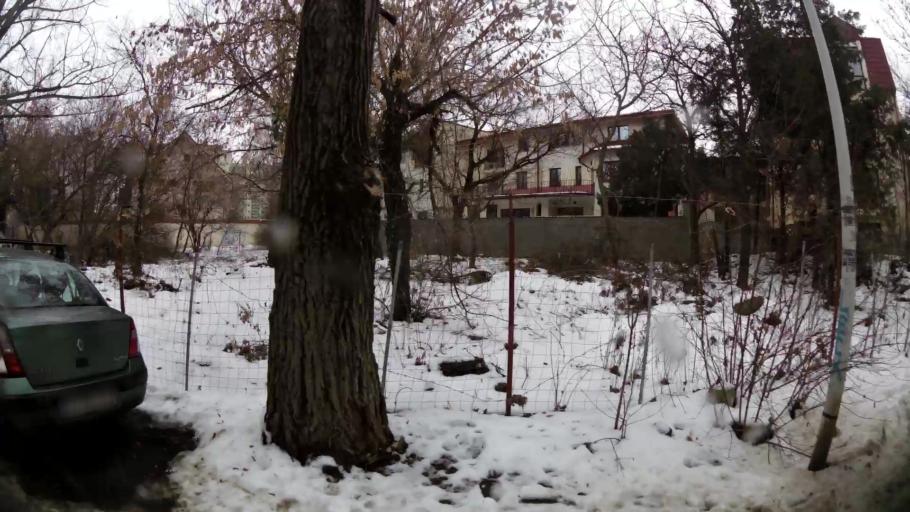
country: RO
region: Ilfov
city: Dobroesti
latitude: 44.4222
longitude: 26.1720
